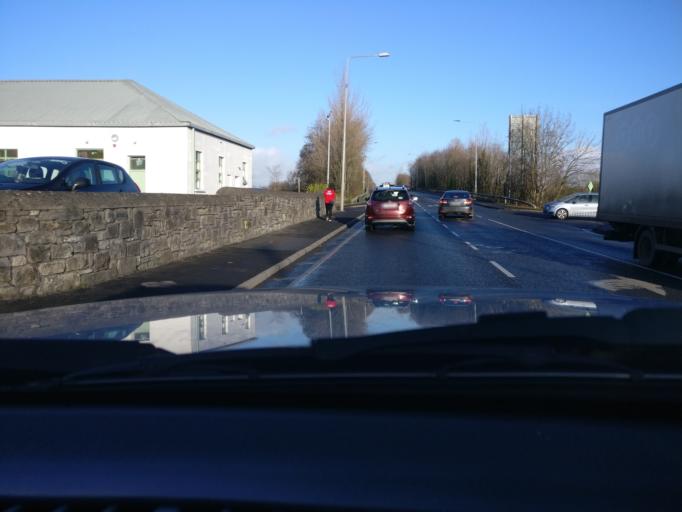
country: IE
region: Leinster
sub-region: An Iarmhi
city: An Muileann gCearr
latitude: 53.5356
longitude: -7.3496
